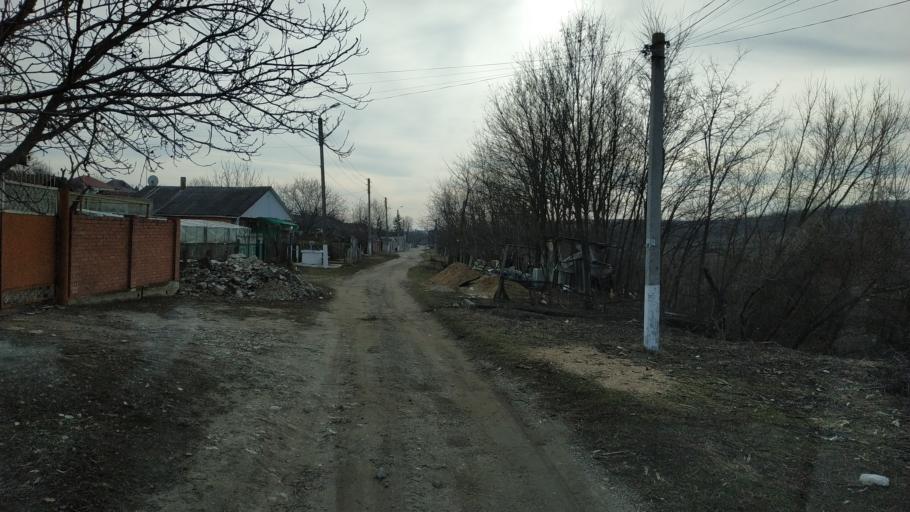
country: MD
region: Chisinau
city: Vatra
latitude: 46.9822
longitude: 28.6722
